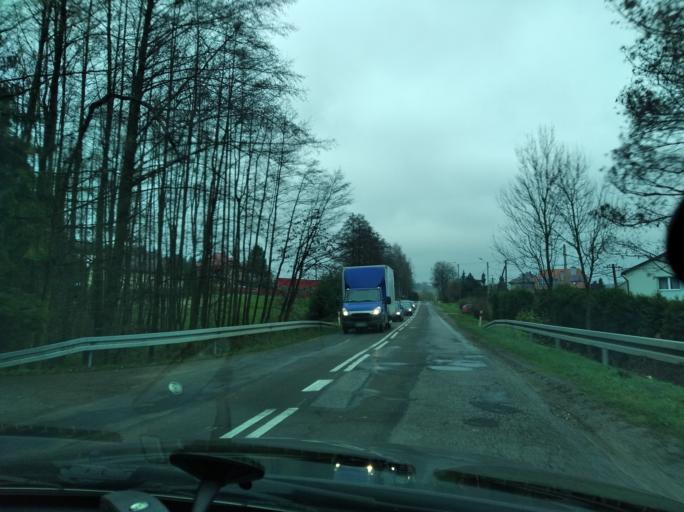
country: PL
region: Subcarpathian Voivodeship
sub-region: Powiat przeworski
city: Jawornik Polski
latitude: 49.8655
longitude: 22.2469
